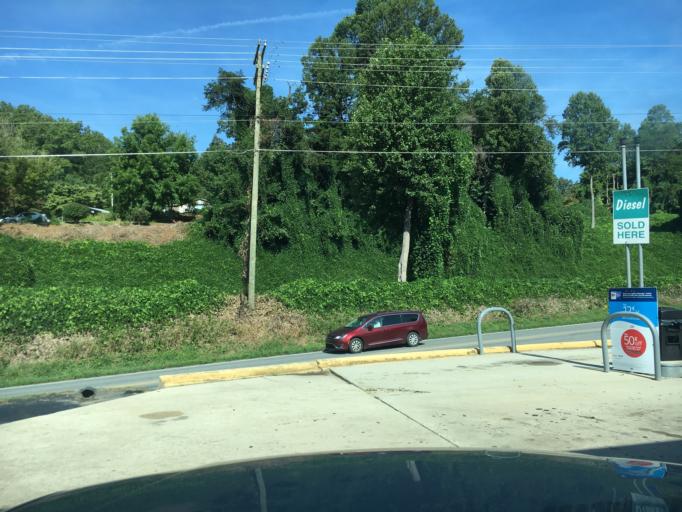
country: US
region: North Carolina
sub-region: Swain County
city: Bryson City
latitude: 35.3956
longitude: -83.4758
